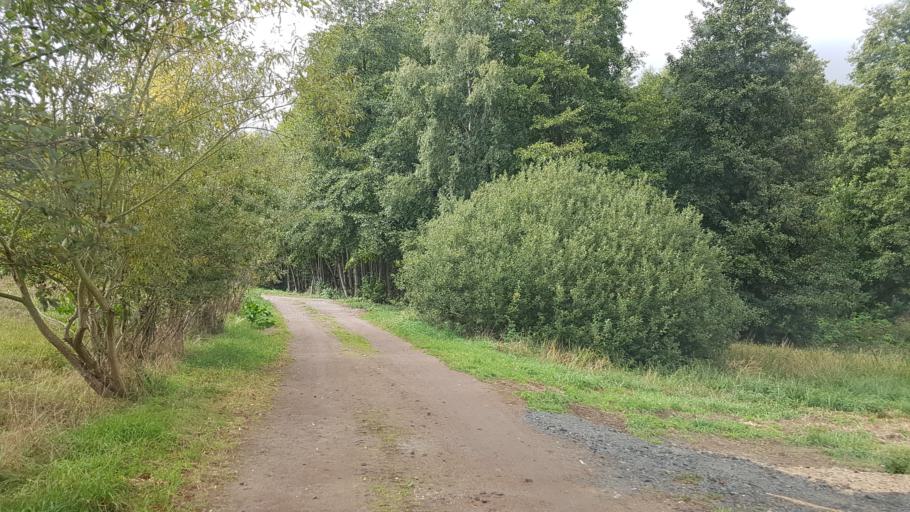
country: DE
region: Saxony
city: Dahlen
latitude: 51.3659
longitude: 13.0112
